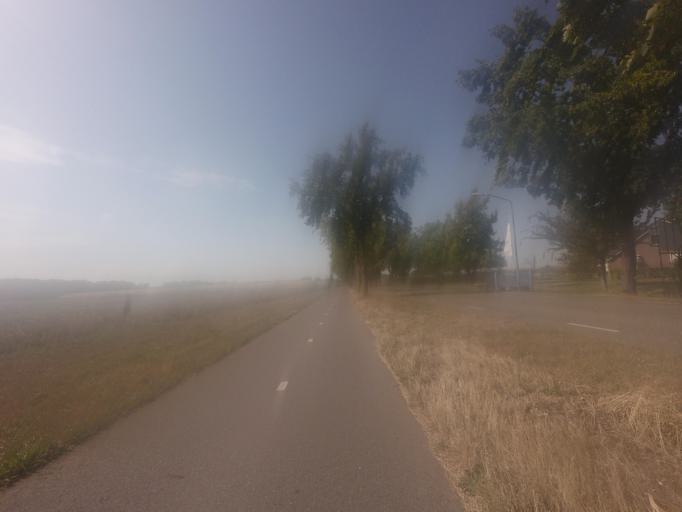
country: NL
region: North Brabant
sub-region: Gemeente Goirle
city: Goirle
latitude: 51.5144
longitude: 5.0826
